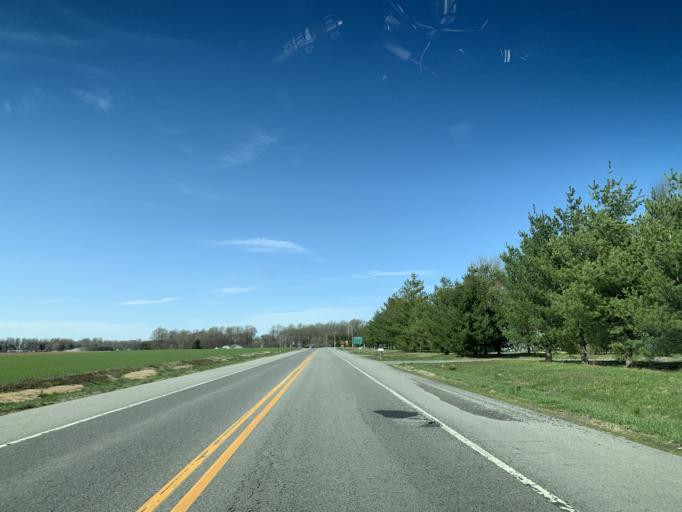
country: US
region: Delaware
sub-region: Sussex County
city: Milford
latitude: 38.9298
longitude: -75.4579
